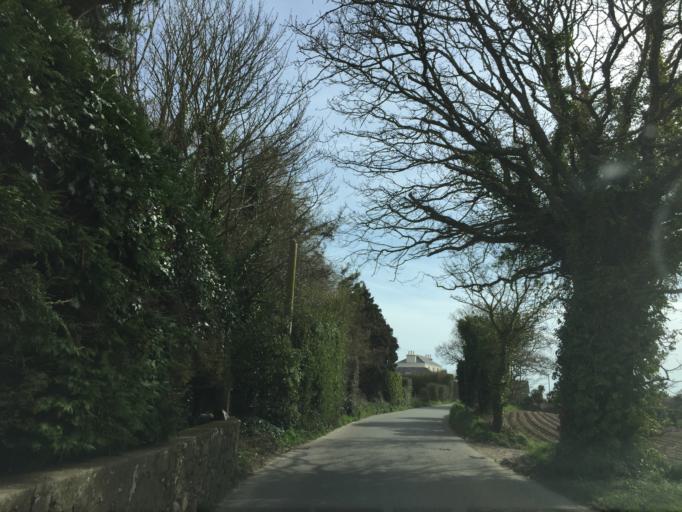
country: JE
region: St Helier
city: Saint Helier
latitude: 49.2284
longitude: -2.0522
